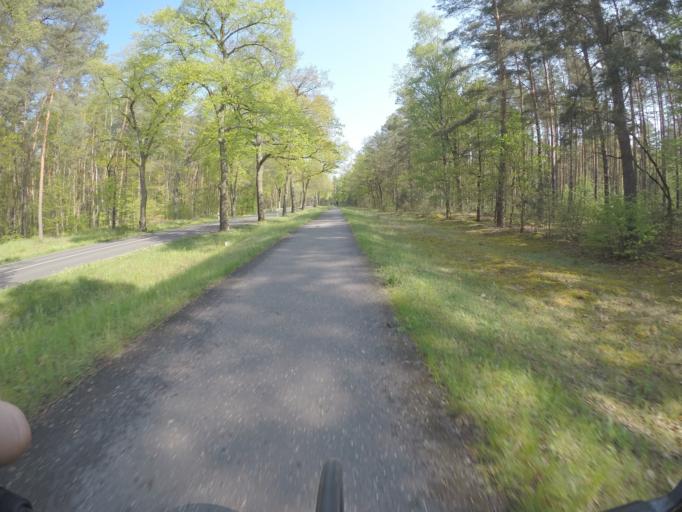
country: DE
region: Brandenburg
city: Wandlitz
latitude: 52.6933
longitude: 13.4428
